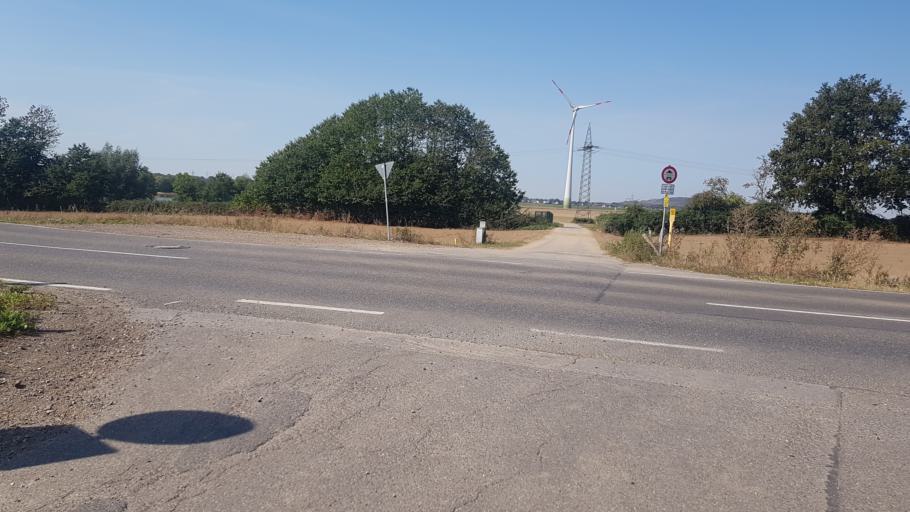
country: DE
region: North Rhine-Westphalia
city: Siersdorf
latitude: 50.8950
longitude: 6.2170
